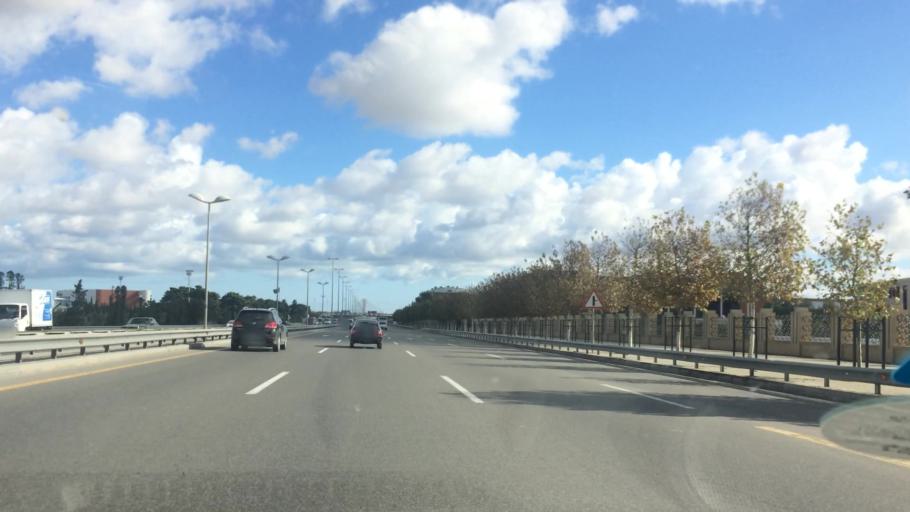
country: AZ
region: Baki
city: Biny Selo
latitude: 40.4531
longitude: 50.0642
